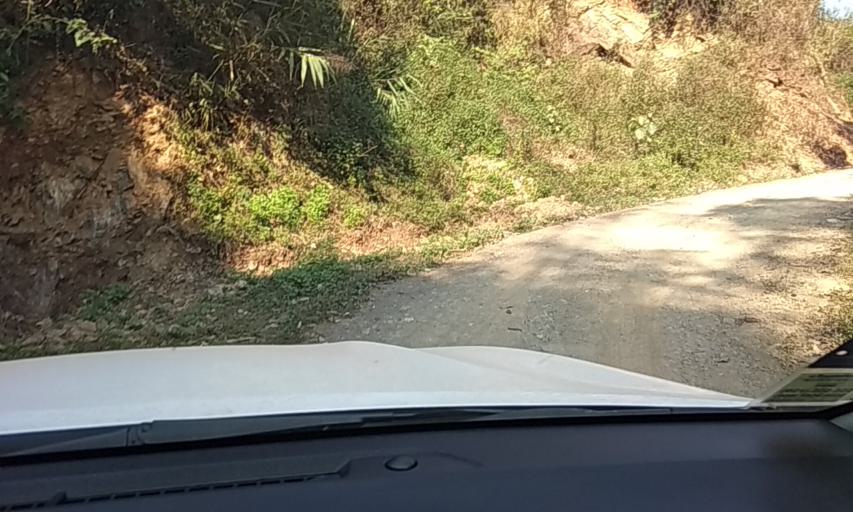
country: LA
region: Phongsali
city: Phongsali
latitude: 21.6970
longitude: 102.0779
